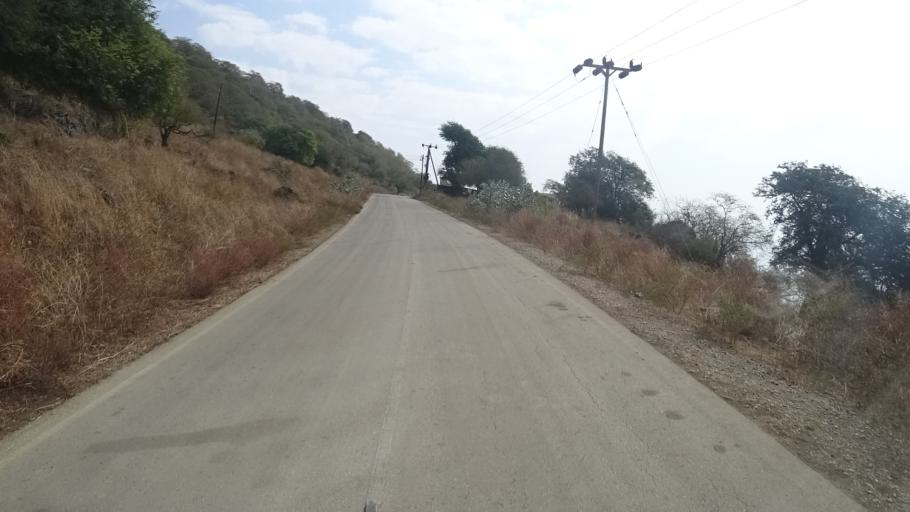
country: YE
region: Al Mahrah
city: Hawf
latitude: 16.7101
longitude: 53.2354
